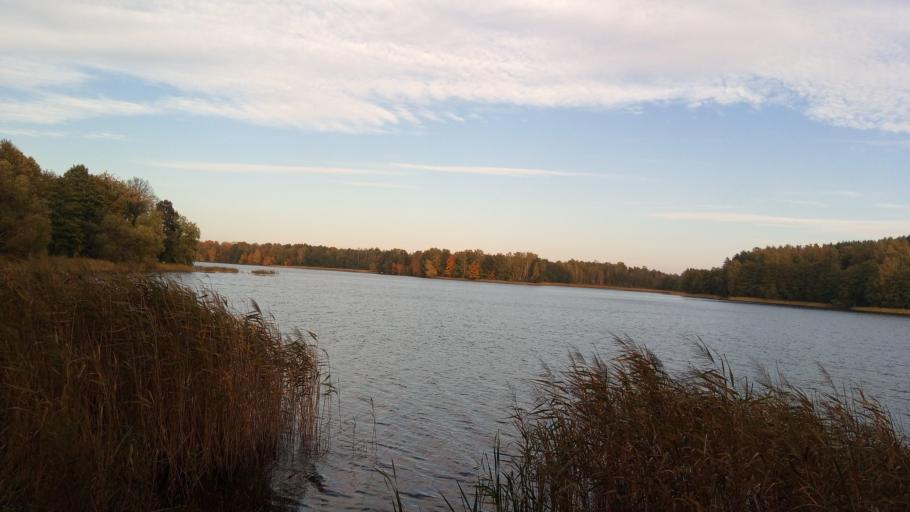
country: LT
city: Trakai
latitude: 54.6346
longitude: 24.9393
